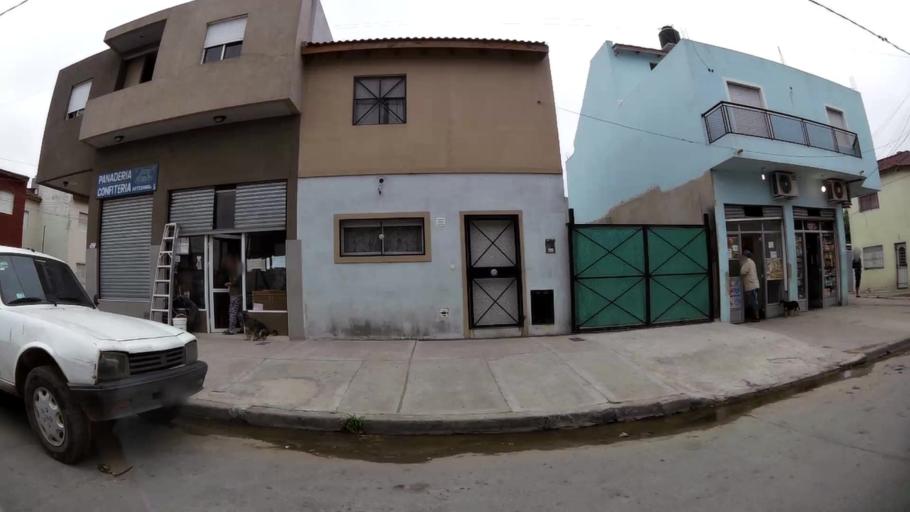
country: AR
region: Buenos Aires
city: San Justo
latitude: -34.6959
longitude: -58.5479
